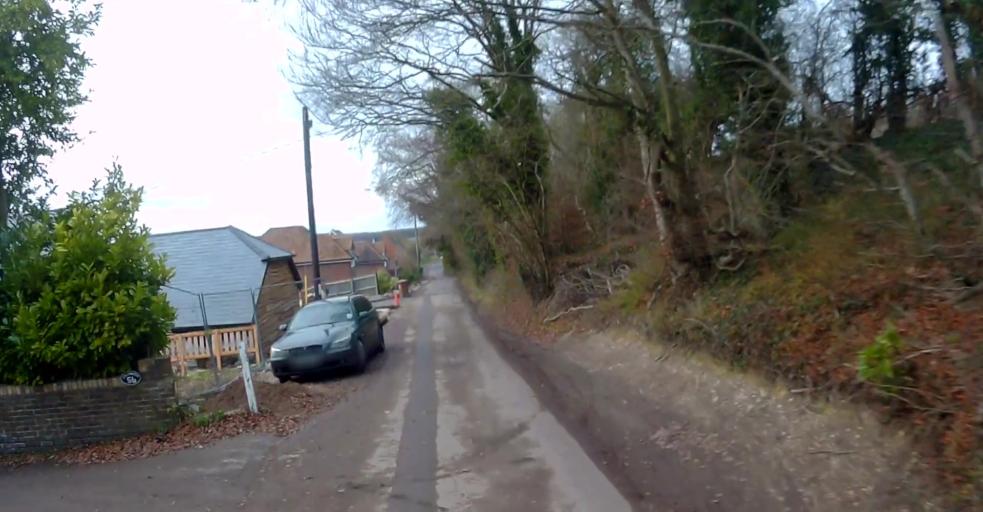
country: GB
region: England
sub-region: Hampshire
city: Overton
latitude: 51.2387
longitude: -1.2565
